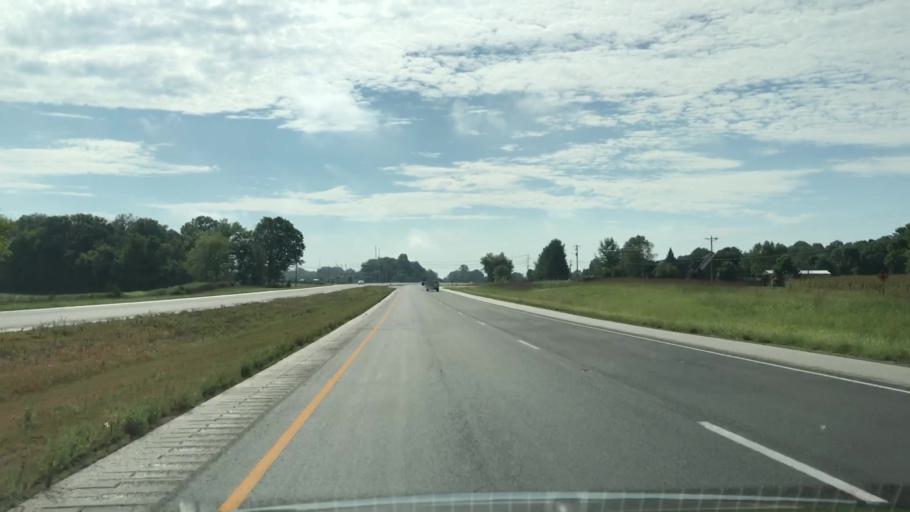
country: US
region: Kentucky
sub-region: Warren County
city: Plano
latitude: 36.8828
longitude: -86.3622
